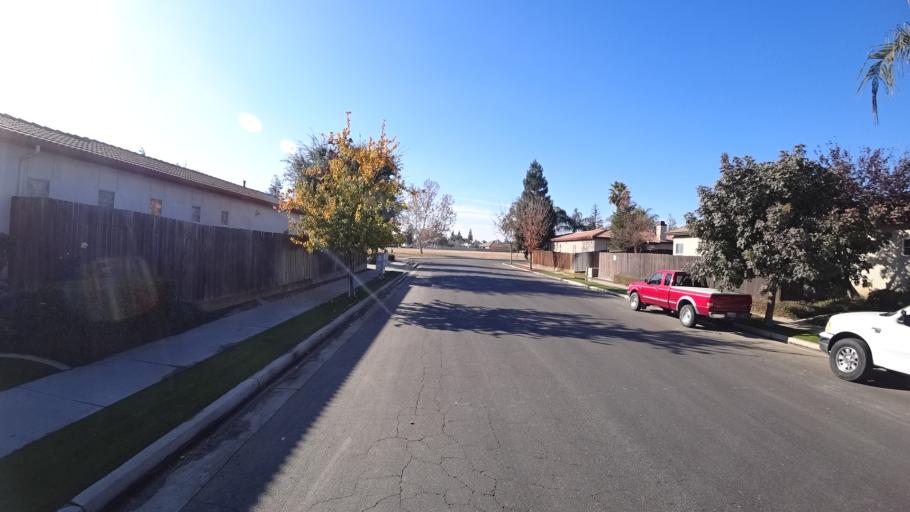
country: US
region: California
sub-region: Kern County
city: Rosedale
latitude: 35.3264
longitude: -119.1324
